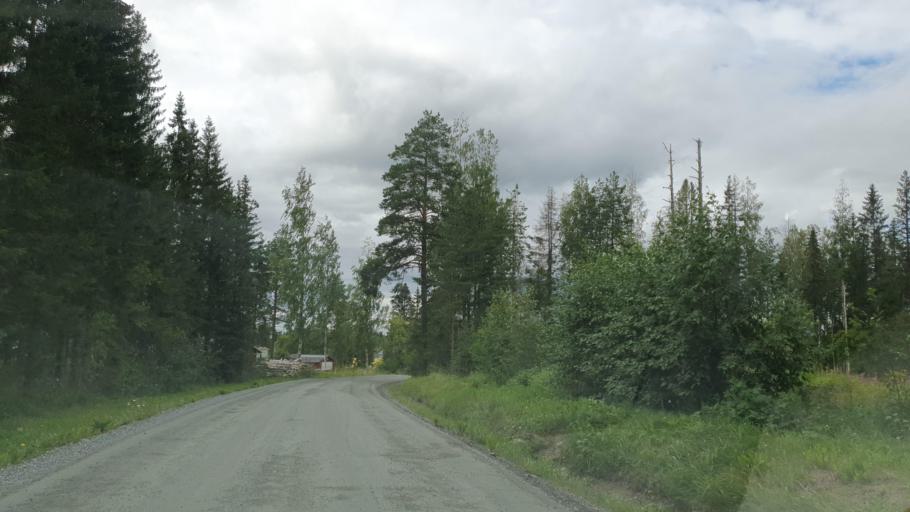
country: FI
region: Northern Savo
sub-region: Ylae-Savo
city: Iisalmi
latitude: 63.5182
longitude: 27.1023
